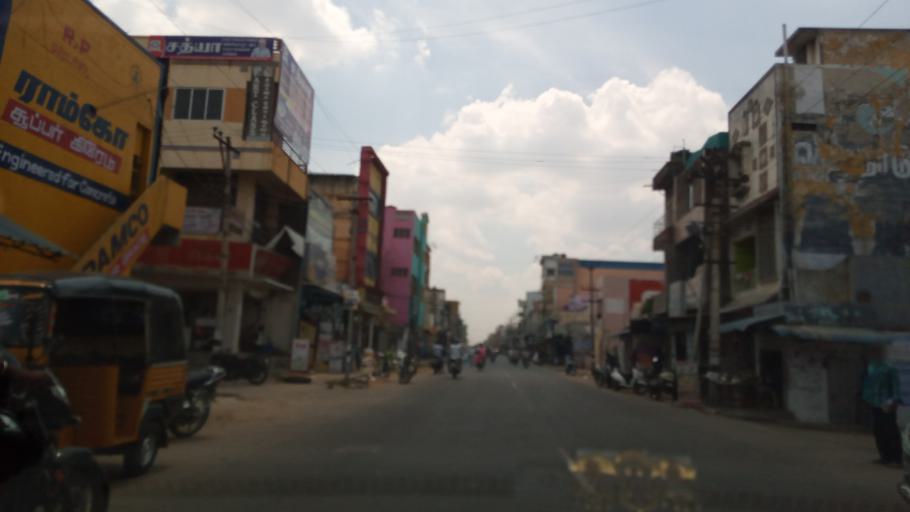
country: IN
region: Tamil Nadu
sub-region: Vellore
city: Walajapet
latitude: 12.9251
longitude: 79.3675
